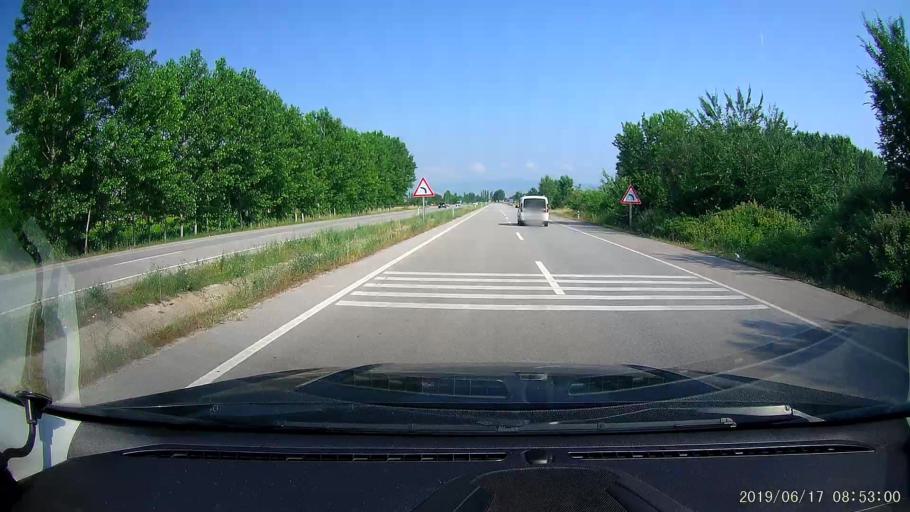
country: TR
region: Tokat
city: Erbaa
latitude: 40.7050
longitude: 36.4880
